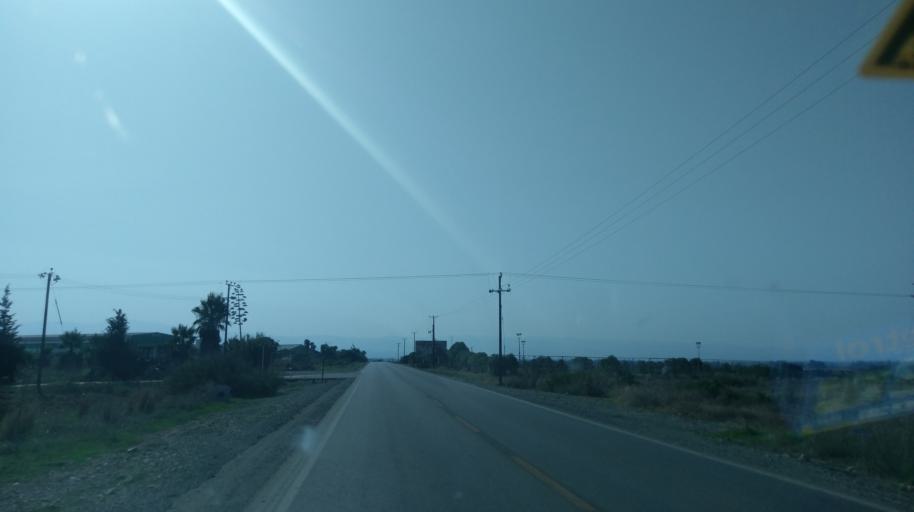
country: CY
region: Lefkosia
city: Morfou
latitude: 35.2328
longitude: 33.0179
